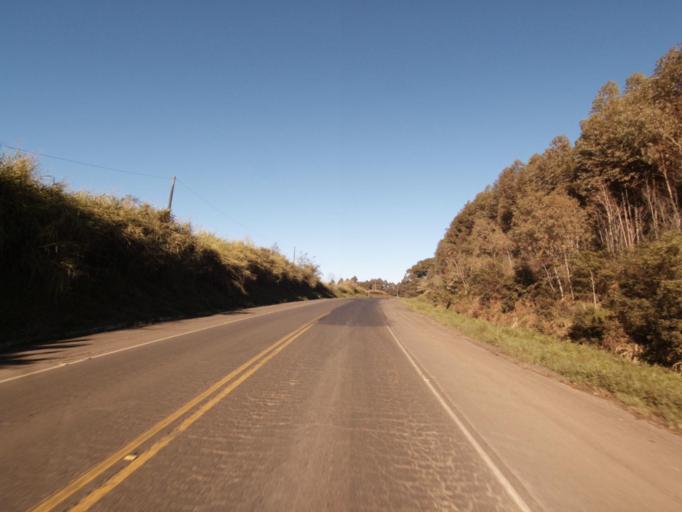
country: BR
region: Rio Grande do Sul
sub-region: Frederico Westphalen
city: Frederico Westphalen
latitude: -26.9143
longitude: -53.1885
